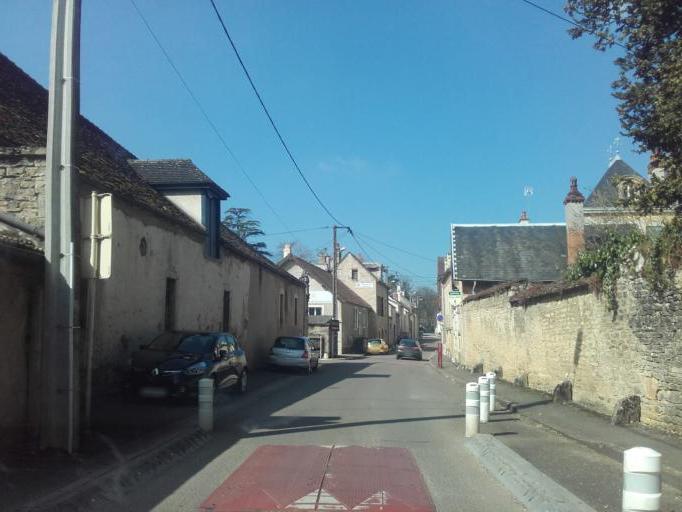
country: FR
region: Bourgogne
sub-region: Departement de la Cote-d'Or
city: Savigny-les-Beaune
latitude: 47.0613
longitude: 4.8224
